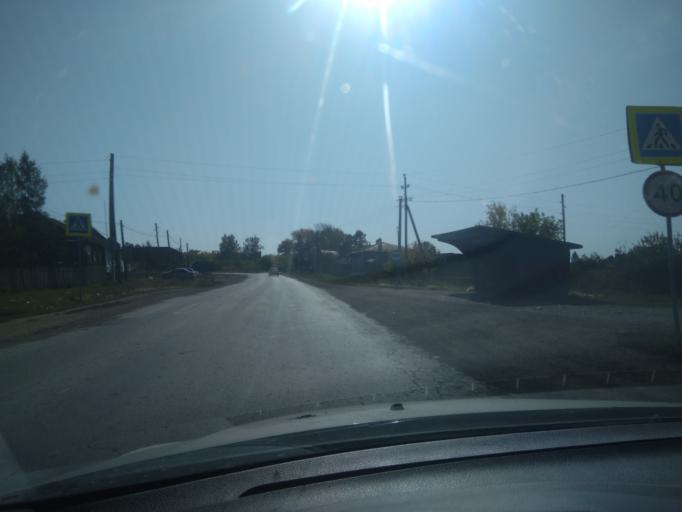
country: RU
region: Sverdlovsk
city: Pokrovskoye
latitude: 56.4669
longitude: 61.6151
